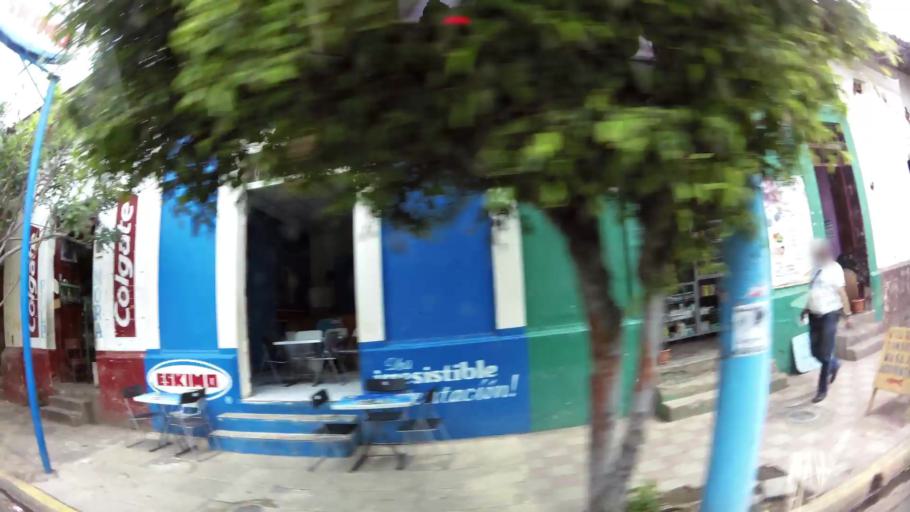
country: NI
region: Rivas
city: Rivas
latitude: 11.4391
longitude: -85.8332
